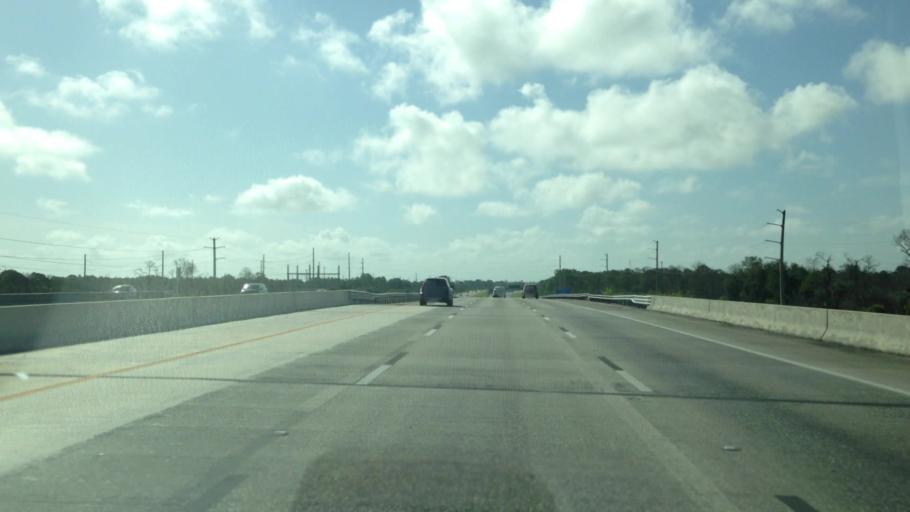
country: US
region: Florida
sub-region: Charlotte County
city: Port Charlotte
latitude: 27.0450
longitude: -82.0687
